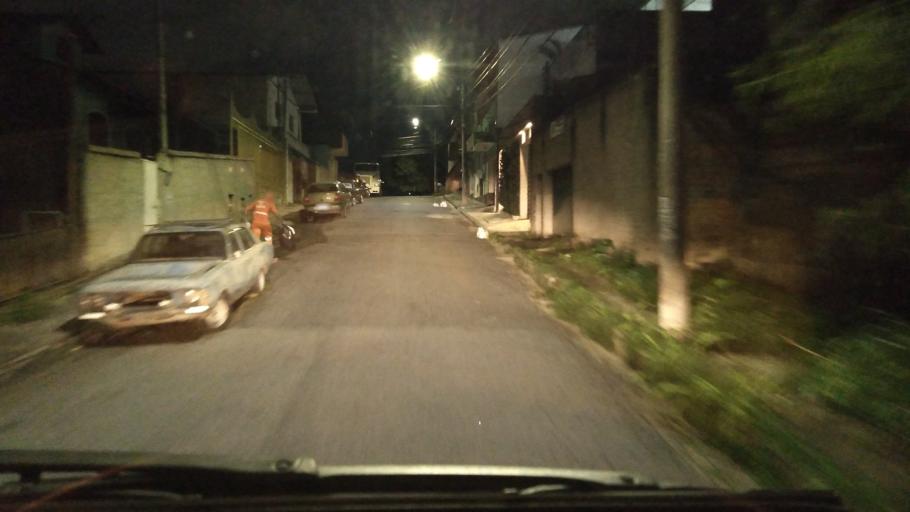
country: BR
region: Minas Gerais
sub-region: Belo Horizonte
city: Belo Horizonte
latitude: -19.9006
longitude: -43.9741
